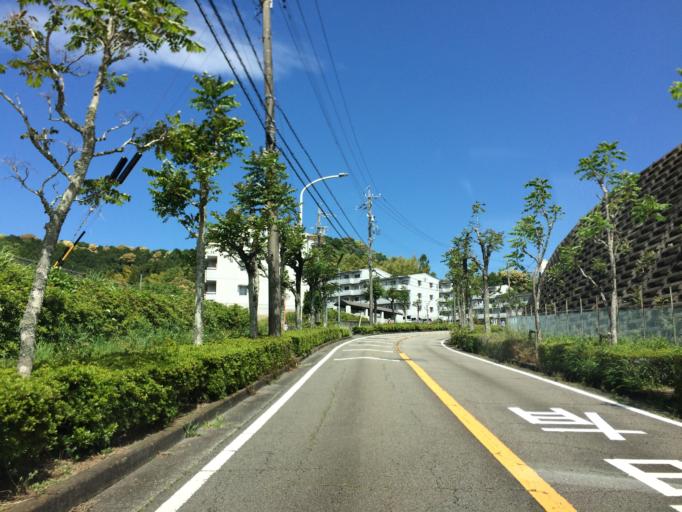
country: JP
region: Shizuoka
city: Fujieda
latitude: 34.8577
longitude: 138.2292
